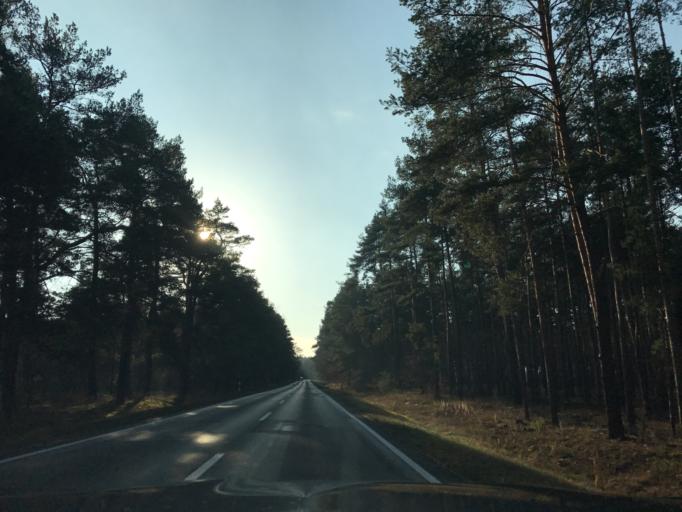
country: DE
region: Brandenburg
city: Wenzlow
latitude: 52.3137
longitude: 12.4782
